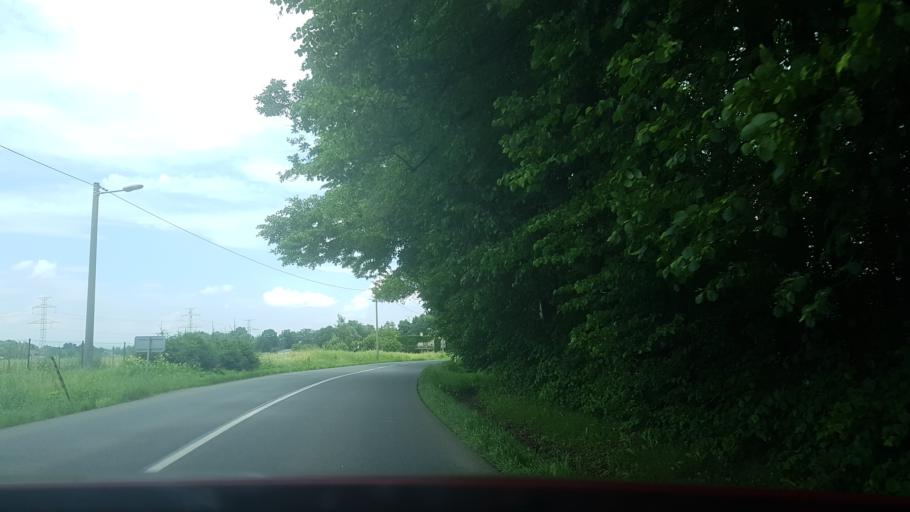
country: CZ
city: Dobra
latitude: 49.6897
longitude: 18.4294
